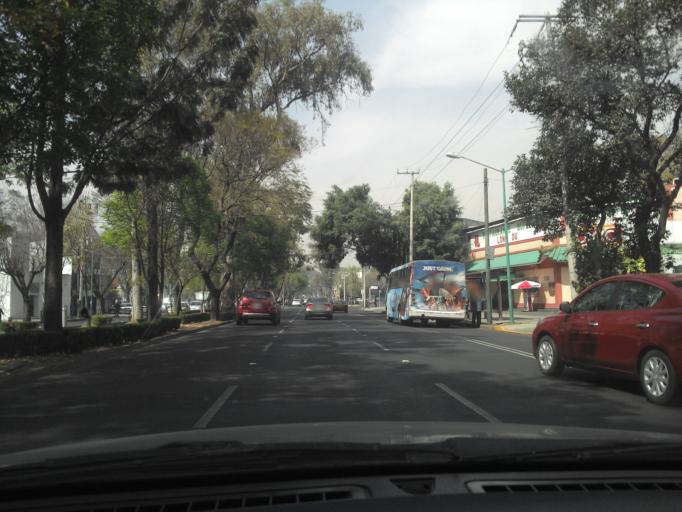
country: MX
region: Mexico City
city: Coyoacan
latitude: 19.3435
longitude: -99.1547
